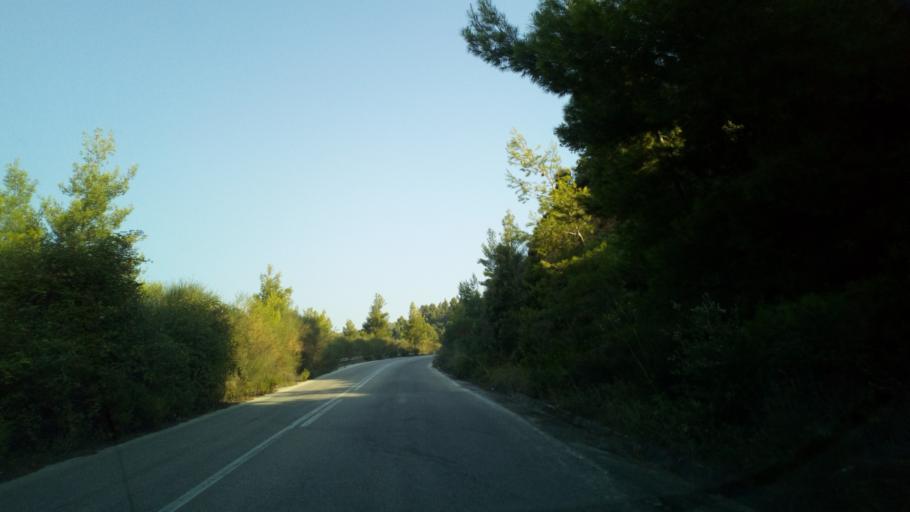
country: GR
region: Central Macedonia
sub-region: Nomos Chalkidikis
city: Neos Marmaras
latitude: 40.1716
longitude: 23.8593
